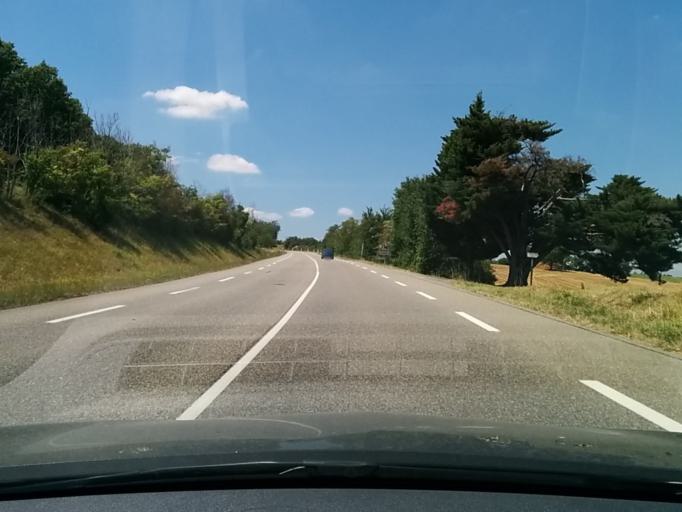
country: FR
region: Midi-Pyrenees
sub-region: Departement du Gers
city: Jegun
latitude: 43.7206
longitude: 0.4143
